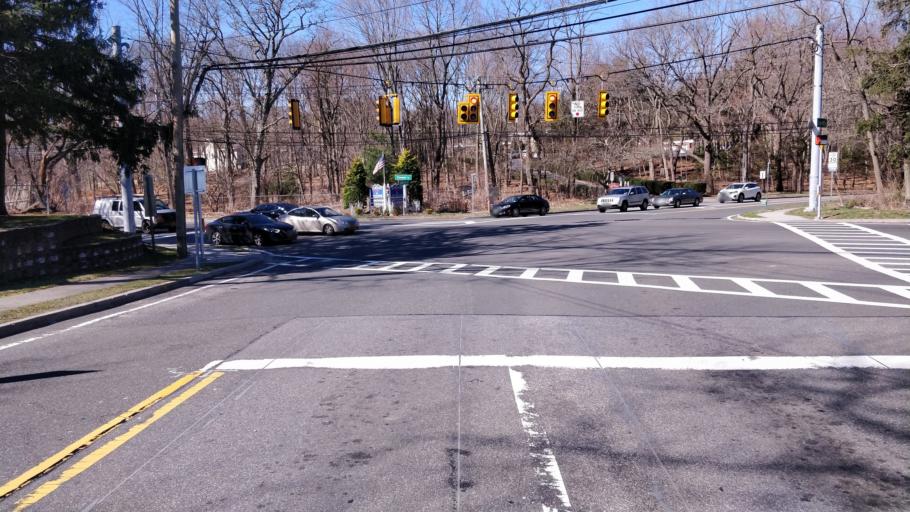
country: US
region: New York
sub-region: Suffolk County
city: Elwood
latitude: 40.8458
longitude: -73.3348
